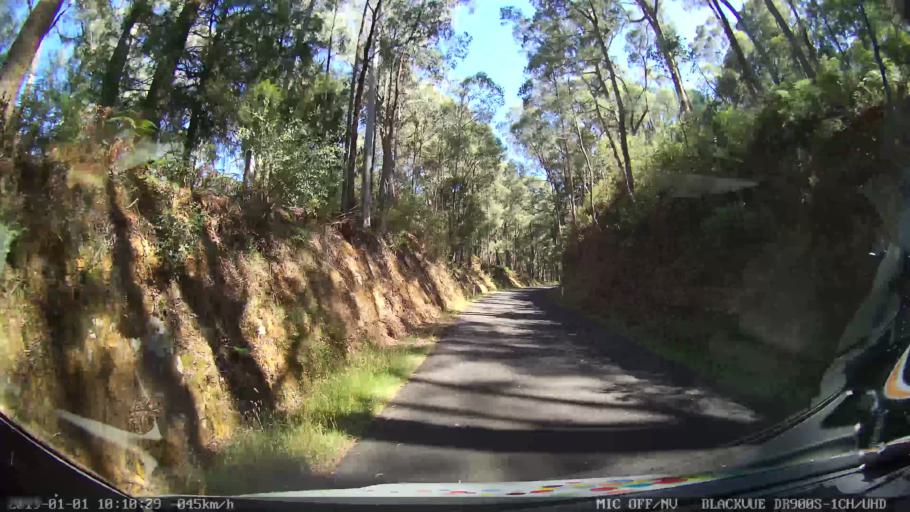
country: AU
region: New South Wales
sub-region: Snowy River
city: Jindabyne
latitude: -36.1409
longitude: 148.1580
